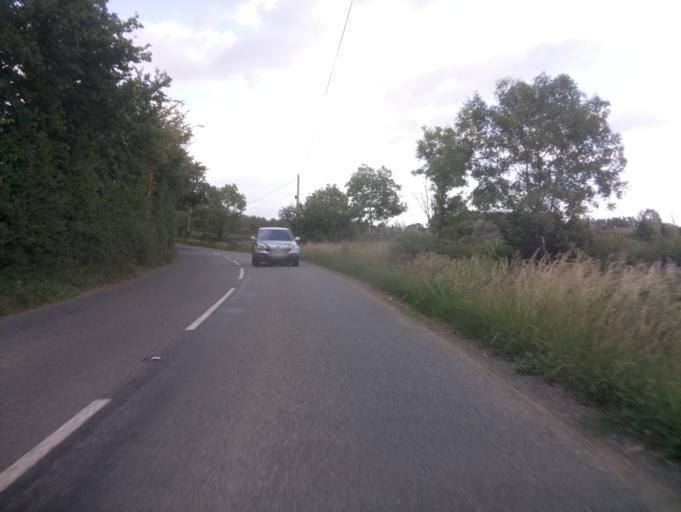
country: GB
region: England
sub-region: Gloucestershire
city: Moreton in Marsh
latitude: 52.0520
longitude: -1.6977
